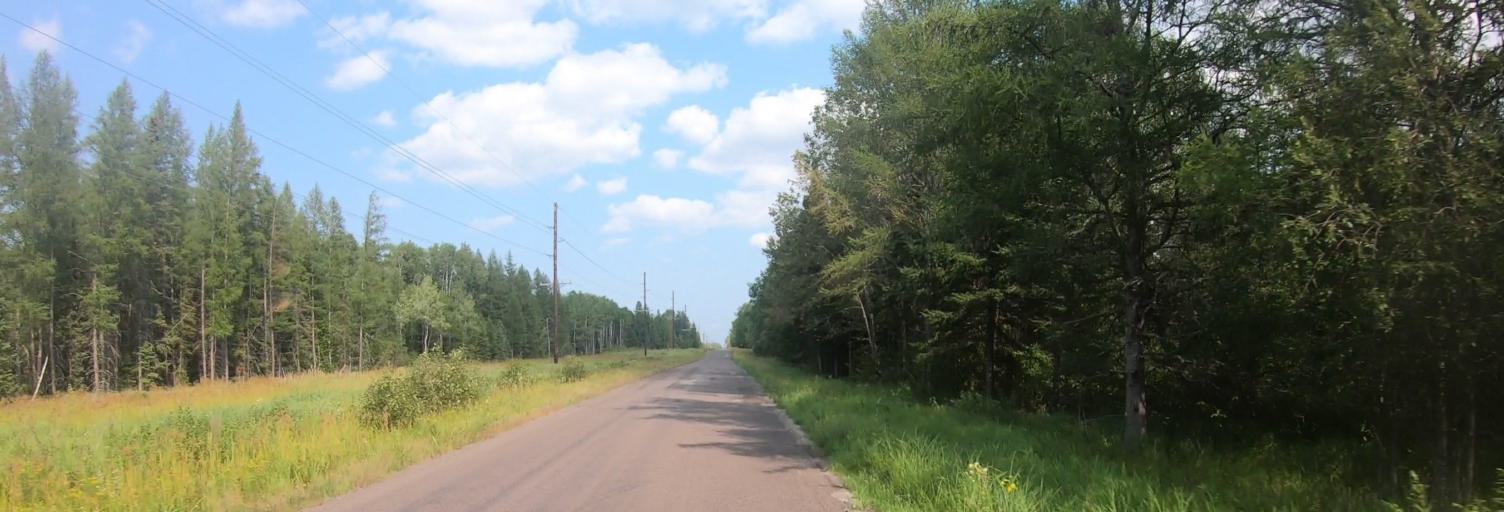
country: US
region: Minnesota
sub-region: Saint Louis County
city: Mountain Iron
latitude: 47.8921
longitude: -92.7363
